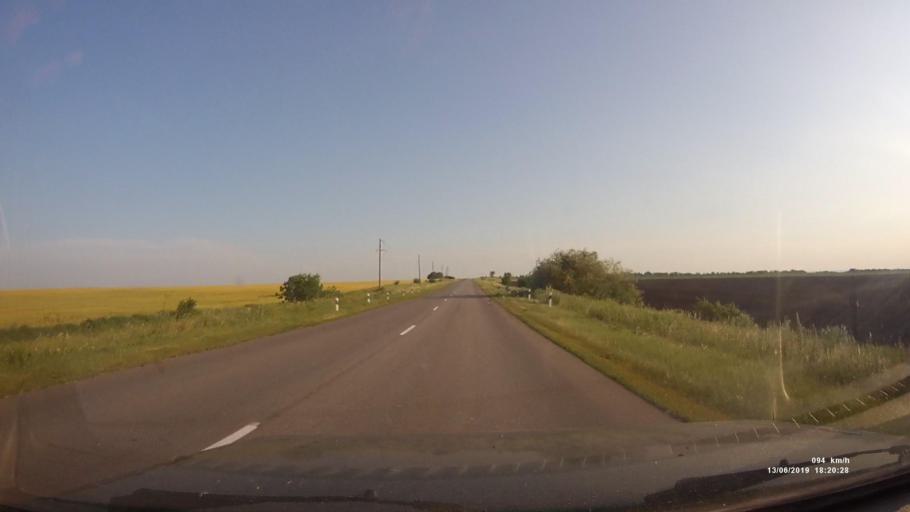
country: RU
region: Rostov
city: Kazanskaya
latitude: 49.8834
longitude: 41.2990
